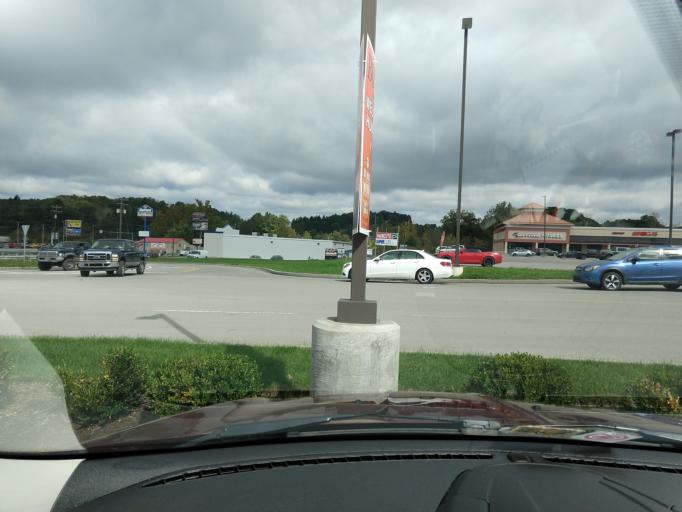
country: US
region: West Virginia
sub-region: Randolph County
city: Elkins
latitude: 38.8953
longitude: -79.8451
